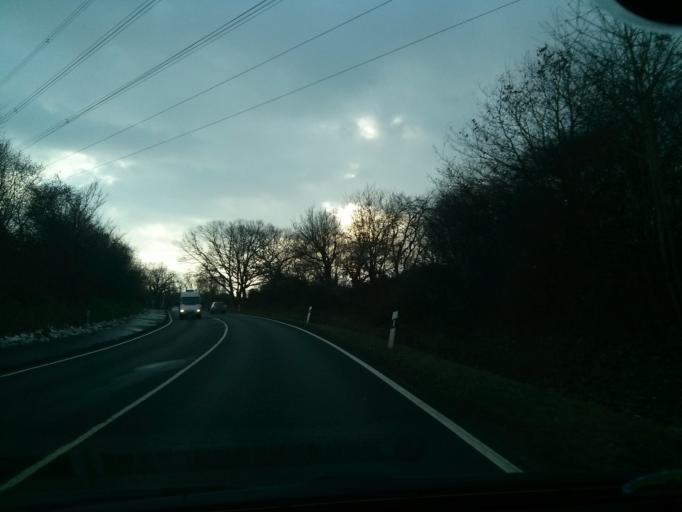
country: DE
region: North Rhine-Westphalia
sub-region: Regierungsbezirk Koln
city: Alfter
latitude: 50.6976
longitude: 7.0093
